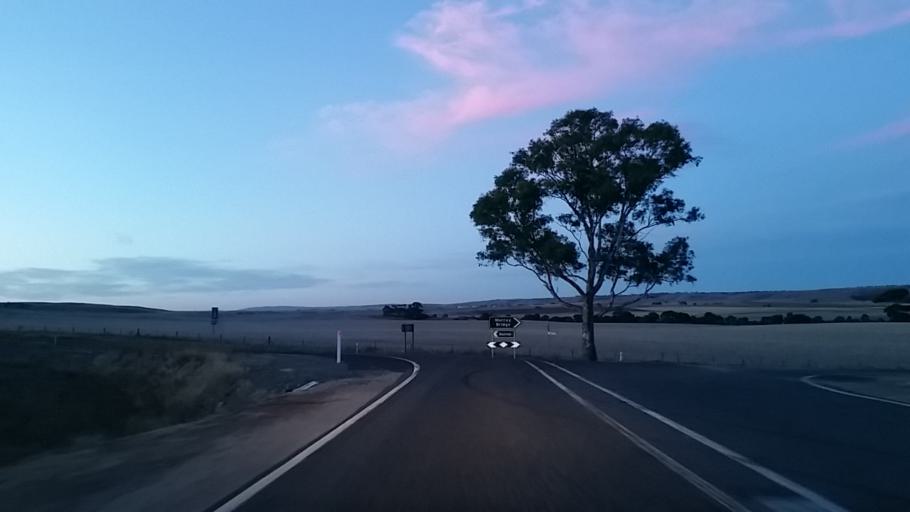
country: AU
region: South Australia
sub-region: Mount Barker
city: Callington
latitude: -35.1078
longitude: 139.0375
